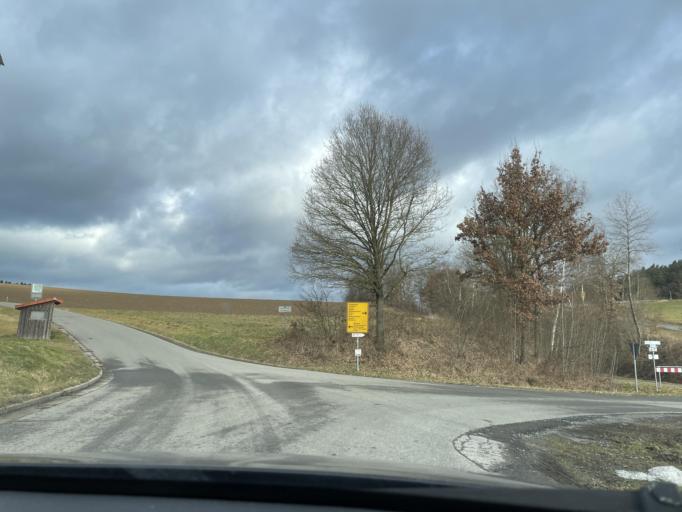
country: DE
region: Bavaria
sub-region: Lower Bavaria
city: Prackenbach
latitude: 49.1146
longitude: 12.8419
